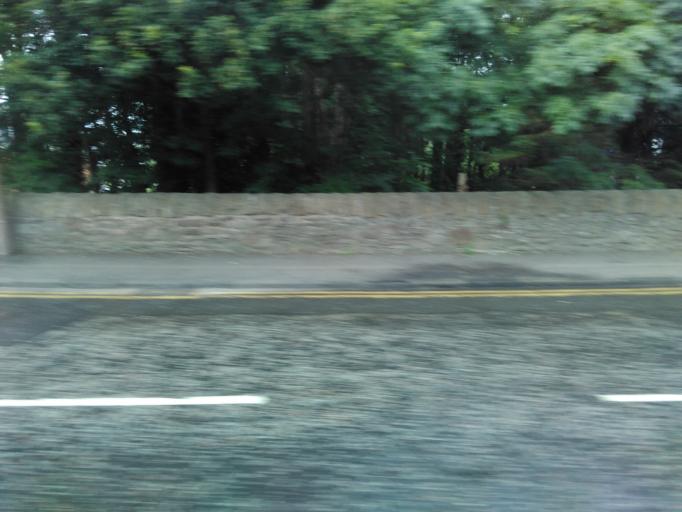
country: GB
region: Scotland
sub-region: Edinburgh
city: Edinburgh
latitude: 55.9242
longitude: -3.1664
